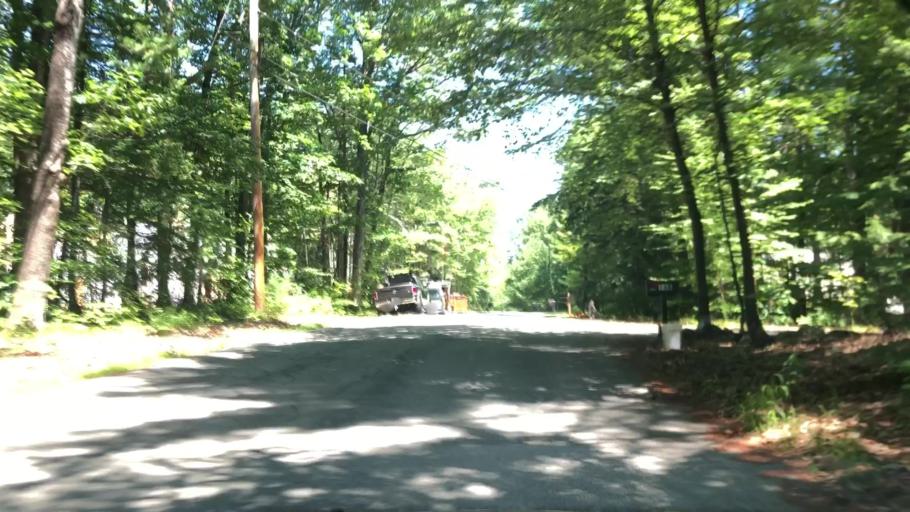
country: US
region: New Hampshire
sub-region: Hillsborough County
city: Milford
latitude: 42.8349
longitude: -71.5866
